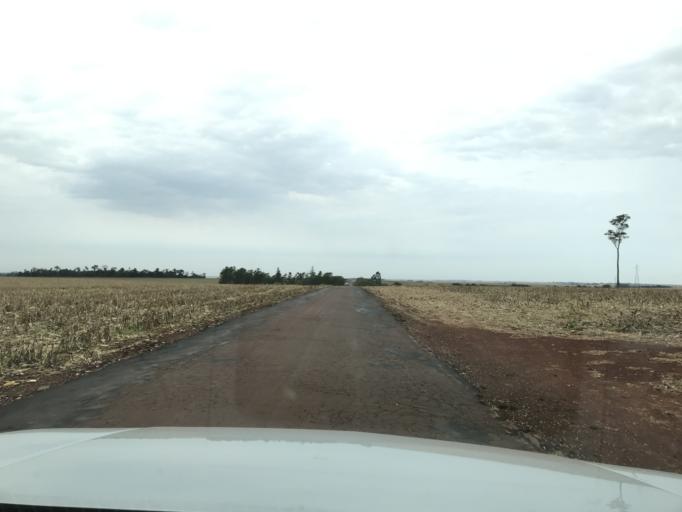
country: BR
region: Parana
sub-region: Palotina
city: Palotina
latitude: -24.2848
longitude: -53.7874
